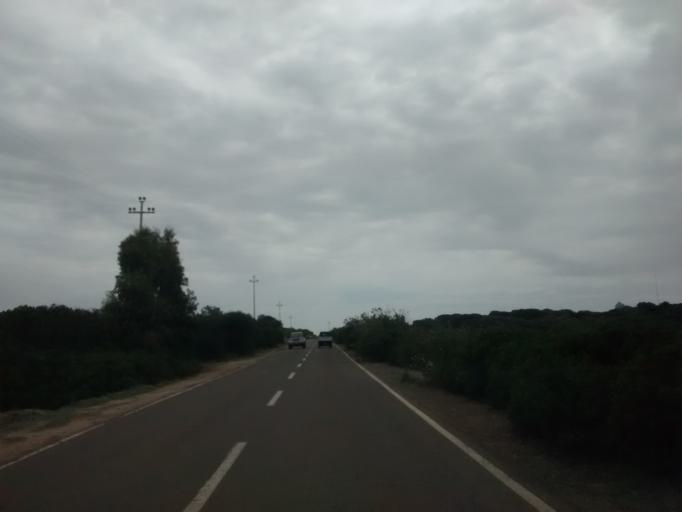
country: IT
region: Sardinia
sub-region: Provincia di Cagliari
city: Villasimius
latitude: 39.1146
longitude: 9.5077
